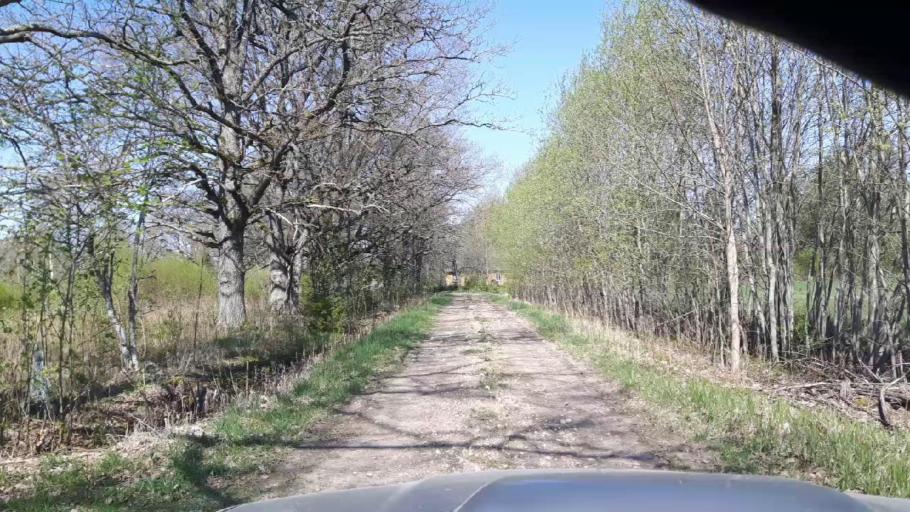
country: EE
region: Paernumaa
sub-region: Tootsi vald
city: Tootsi
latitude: 58.4623
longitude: 24.7879
